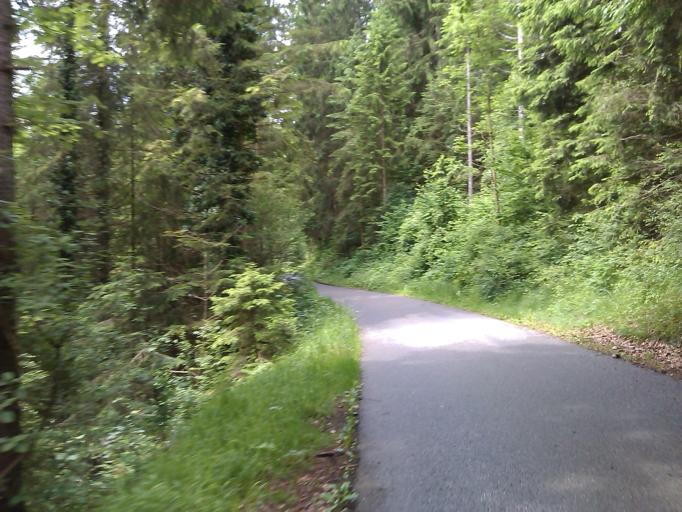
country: AT
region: Tyrol
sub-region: Politischer Bezirk Reutte
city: Pflach
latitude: 47.5046
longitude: 10.7070
